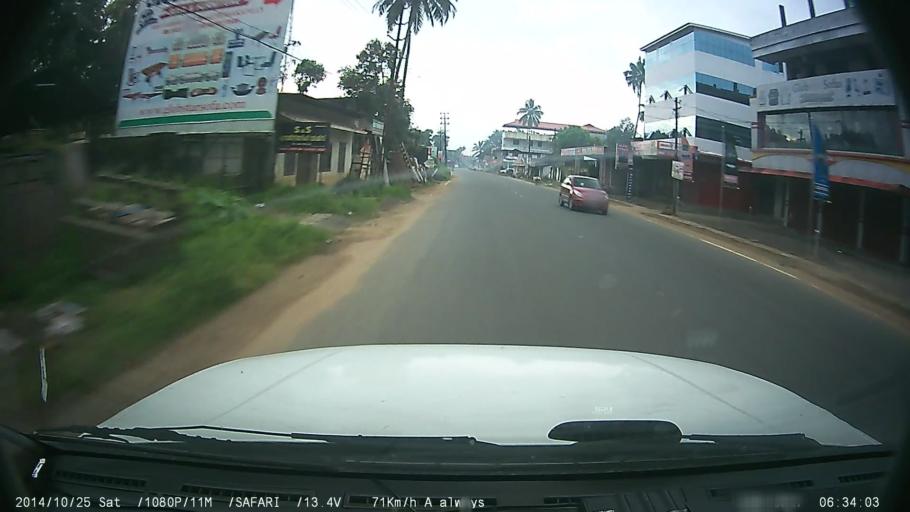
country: IN
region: Kerala
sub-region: Ernakulam
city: Muvattupula
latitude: 10.0133
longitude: 76.5672
